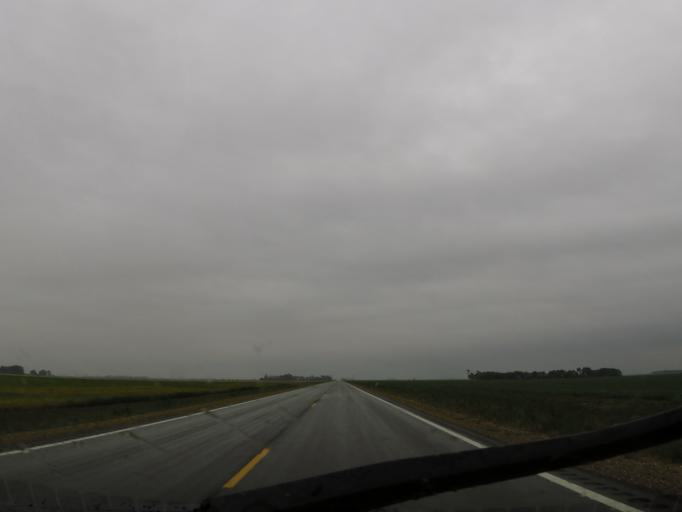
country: US
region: Minnesota
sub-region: Kittson County
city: Hallock
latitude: 48.4568
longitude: -97.0373
